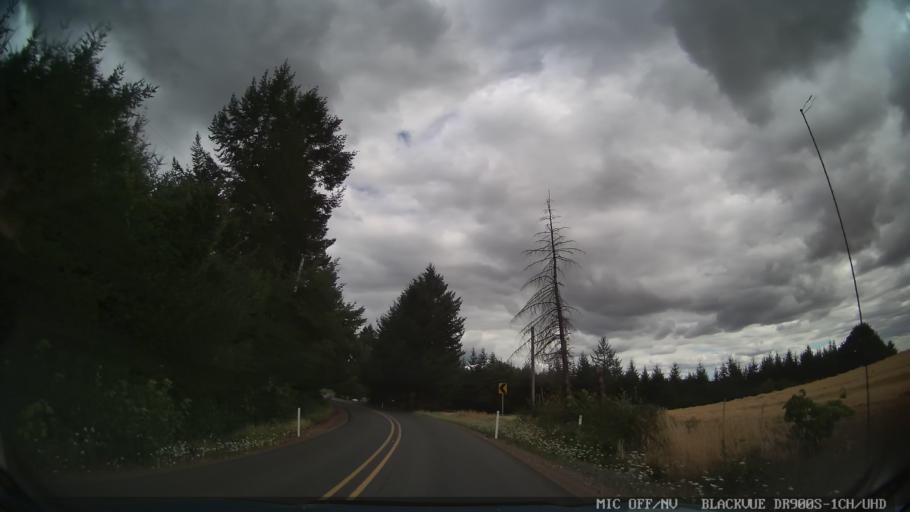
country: US
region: Oregon
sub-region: Linn County
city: Lyons
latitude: 44.8521
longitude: -122.6787
